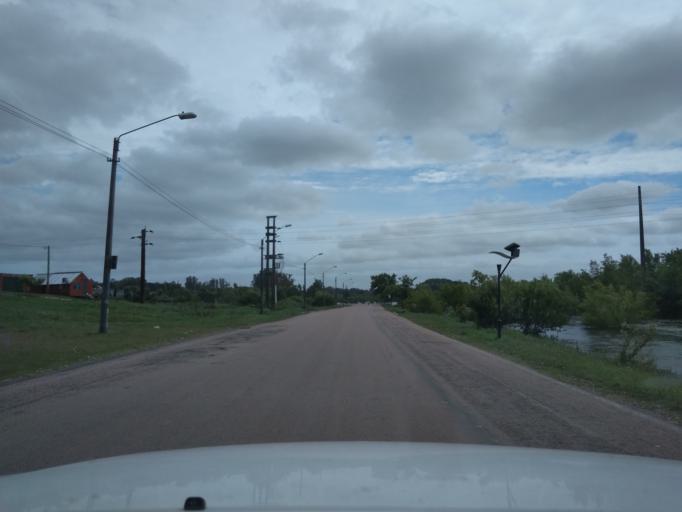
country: UY
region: Florida
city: Florida
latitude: -34.1065
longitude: -56.2050
